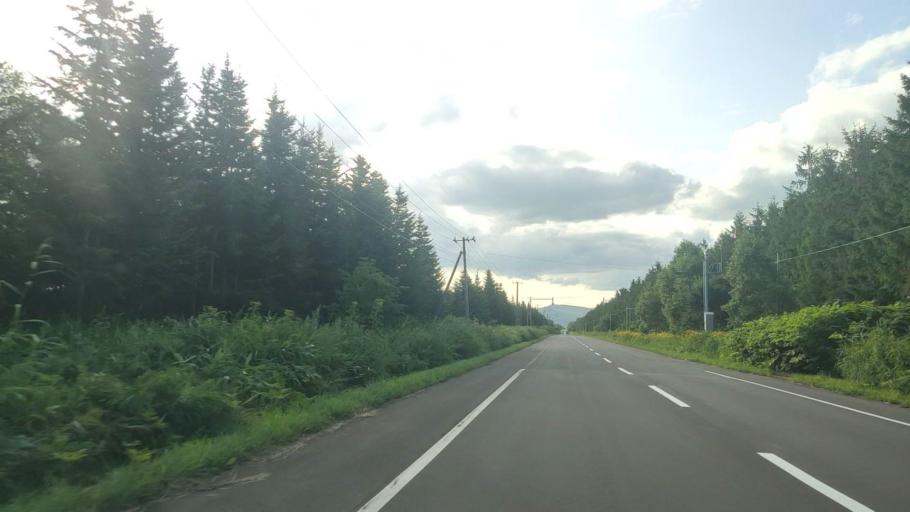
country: JP
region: Hokkaido
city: Makubetsu
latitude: 44.8859
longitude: 142.0102
